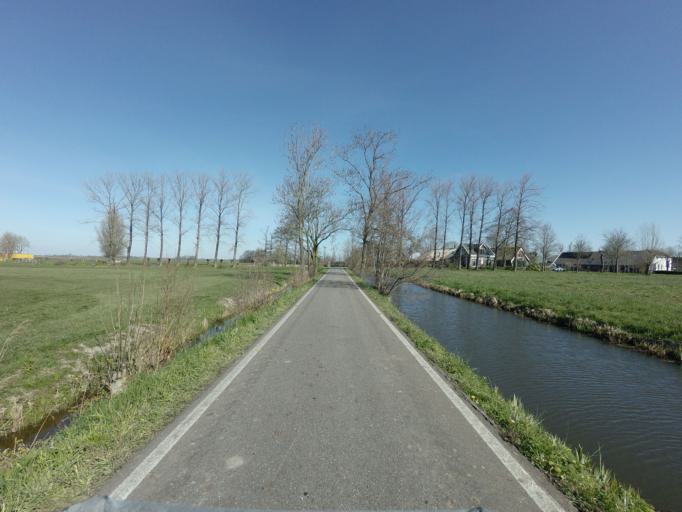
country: NL
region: Utrecht
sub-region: Gemeente Woerden
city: Woerden
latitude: 52.1057
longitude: 4.9325
